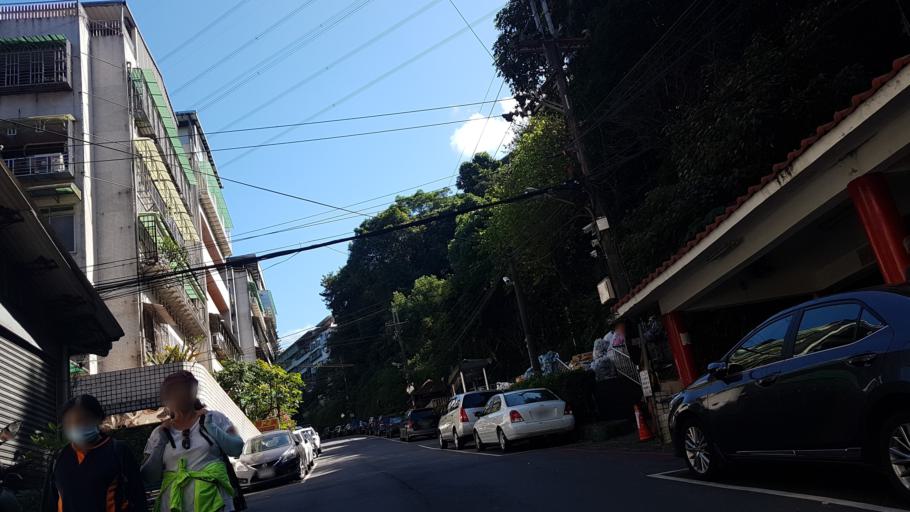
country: TW
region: Taipei
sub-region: Taipei
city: Banqiao
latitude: 24.9493
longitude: 121.5297
